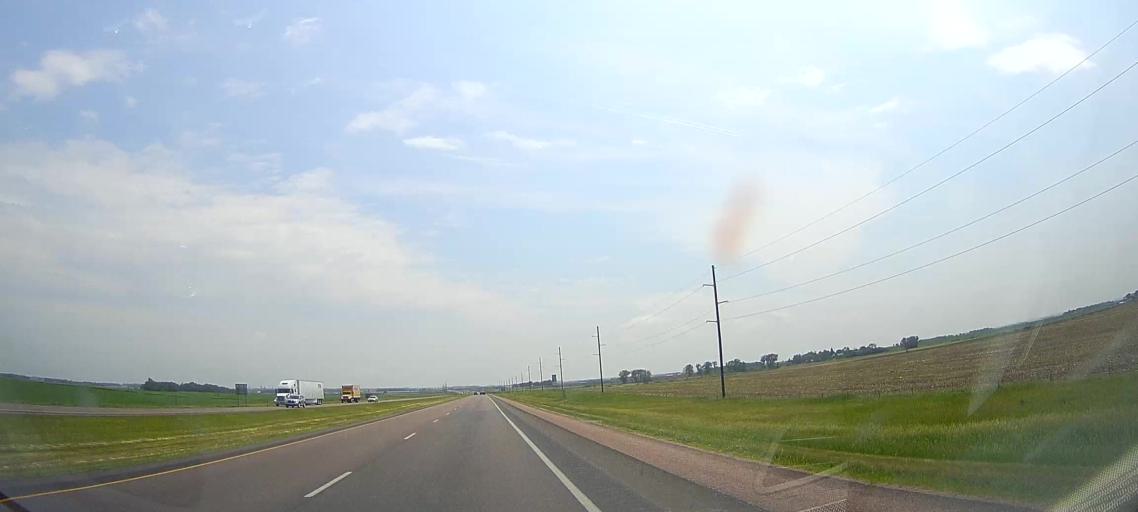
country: US
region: South Dakota
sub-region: Union County
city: Beresford
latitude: 43.1520
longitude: -96.7959
